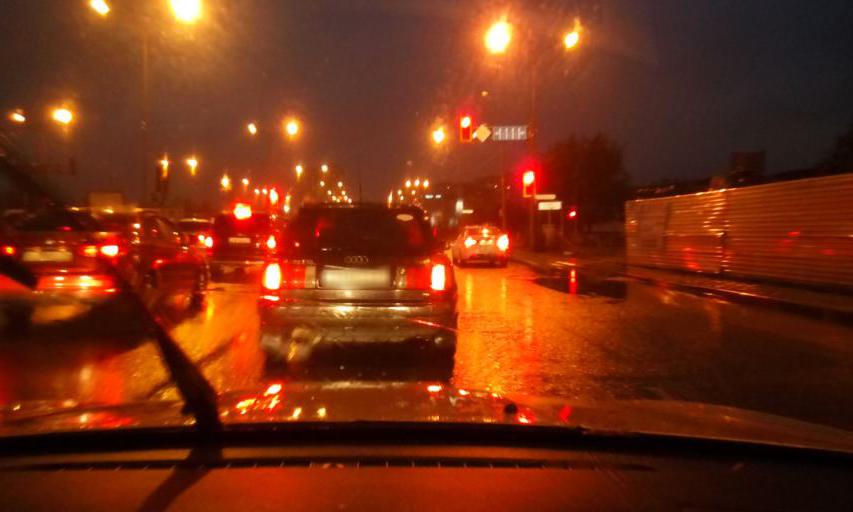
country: KZ
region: Astana Qalasy
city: Astana
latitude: 51.1767
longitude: 71.3929
